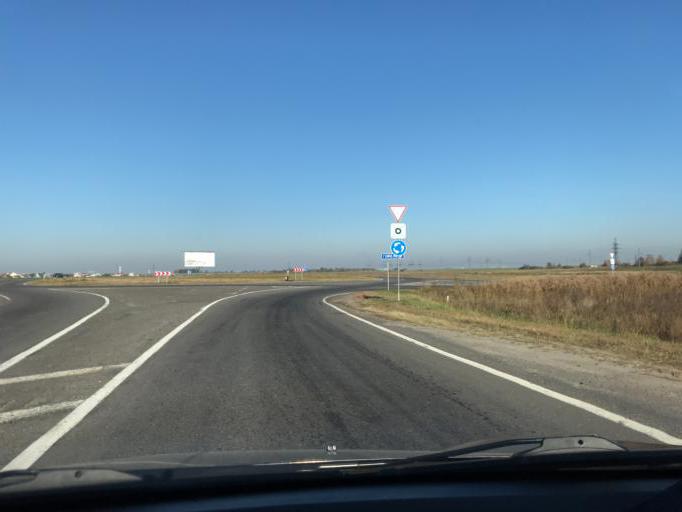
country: BY
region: Gomel
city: Kastsyukowka
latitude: 52.4514
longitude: 30.8249
